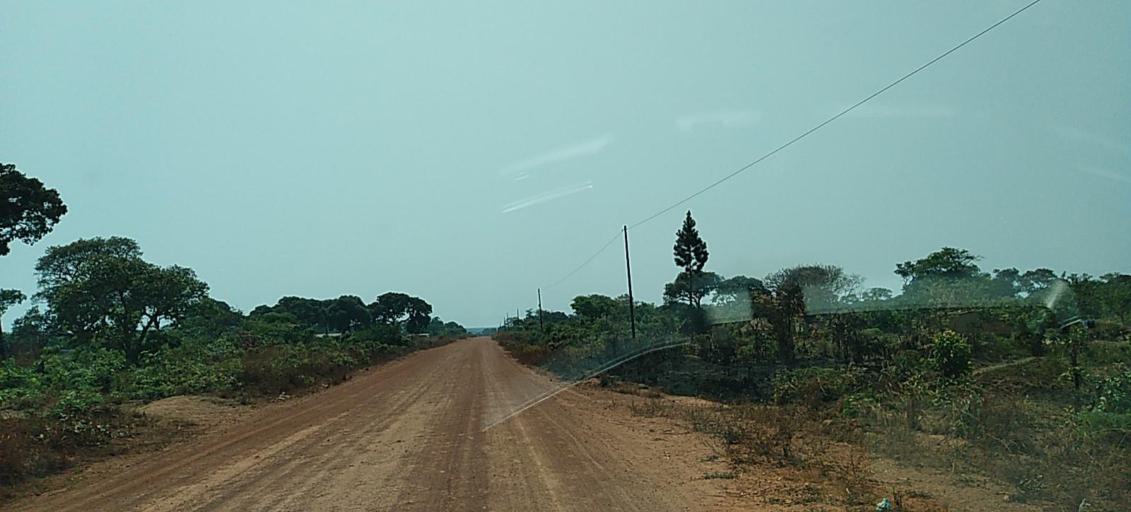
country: ZM
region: North-Western
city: Kansanshi
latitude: -11.9968
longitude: 26.6034
